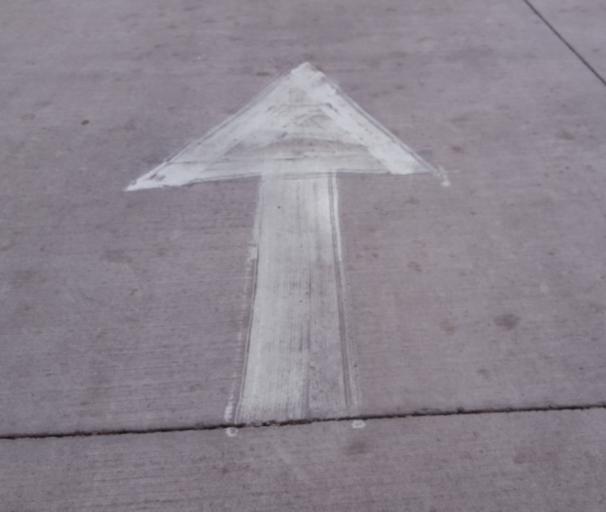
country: US
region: Illinois
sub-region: Cook County
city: Winnetka
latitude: 42.1055
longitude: -87.7333
